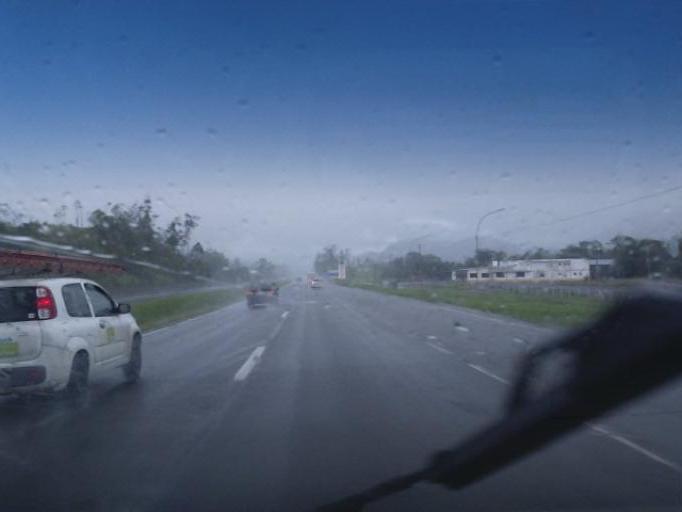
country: BR
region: Sao Paulo
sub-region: Miracatu
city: Miracatu
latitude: -24.2725
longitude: -47.4055
